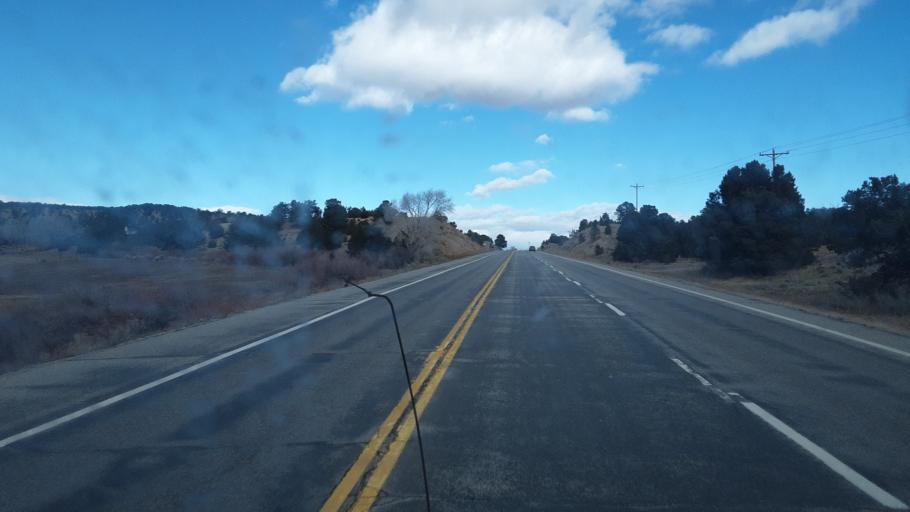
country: US
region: Colorado
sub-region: Chaffee County
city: Salida
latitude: 38.6707
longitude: -106.0906
